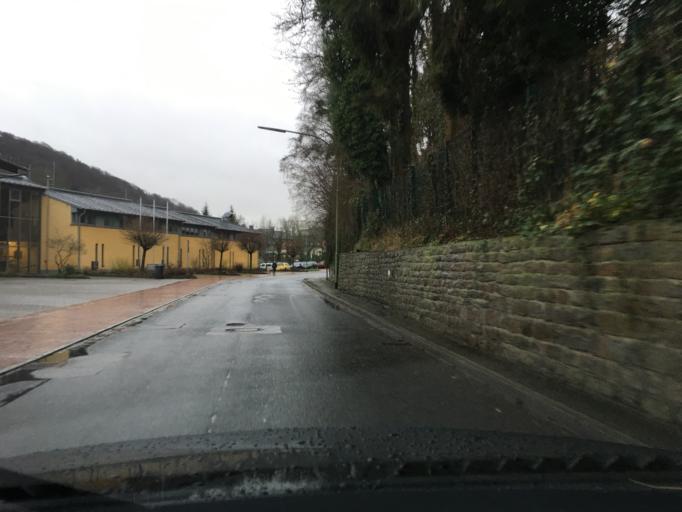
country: DE
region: North Rhine-Westphalia
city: Hattingen
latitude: 51.3562
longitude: 7.1214
